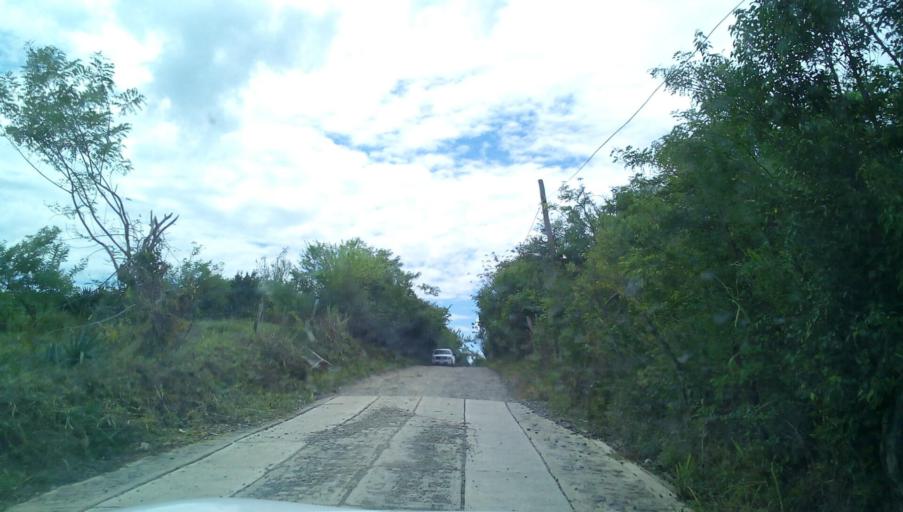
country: MX
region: Veracruz
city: Tepetzintla
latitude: 21.1567
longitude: -97.8524
